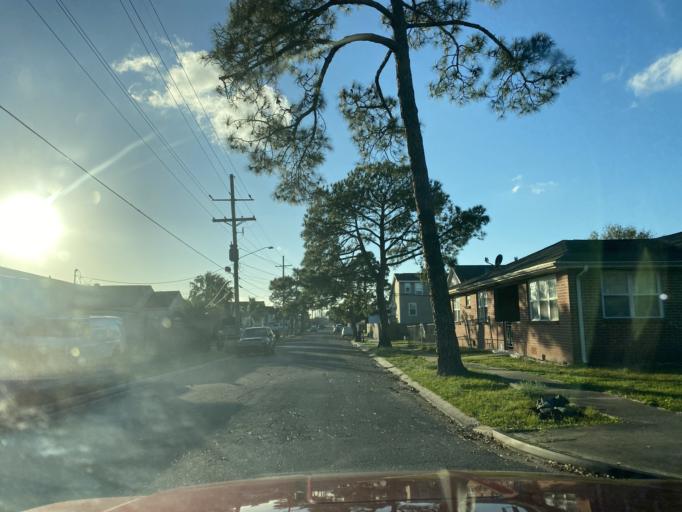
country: US
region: Louisiana
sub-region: Orleans Parish
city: New Orleans
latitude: 30.0194
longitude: -90.0517
